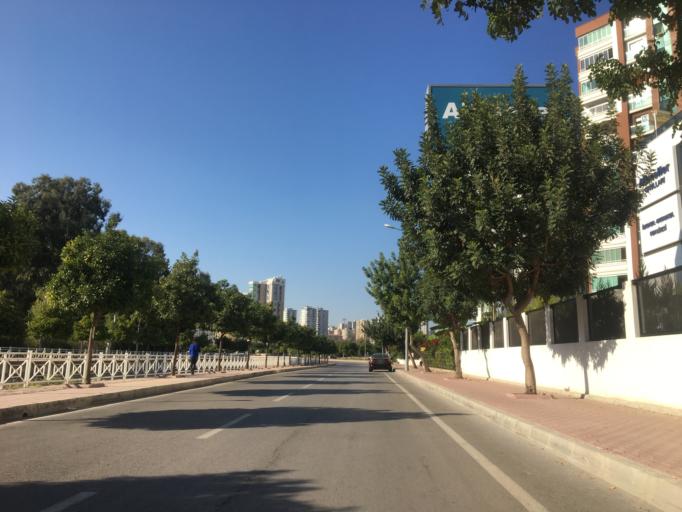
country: TR
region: Adana
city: Seyhan
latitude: 37.0276
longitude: 35.2724
